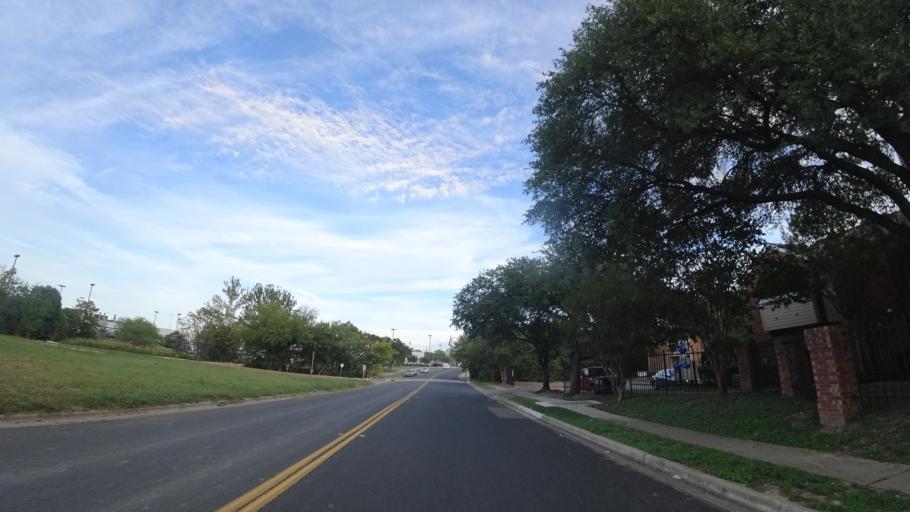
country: US
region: Texas
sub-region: Travis County
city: Austin
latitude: 30.2037
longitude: -97.7634
